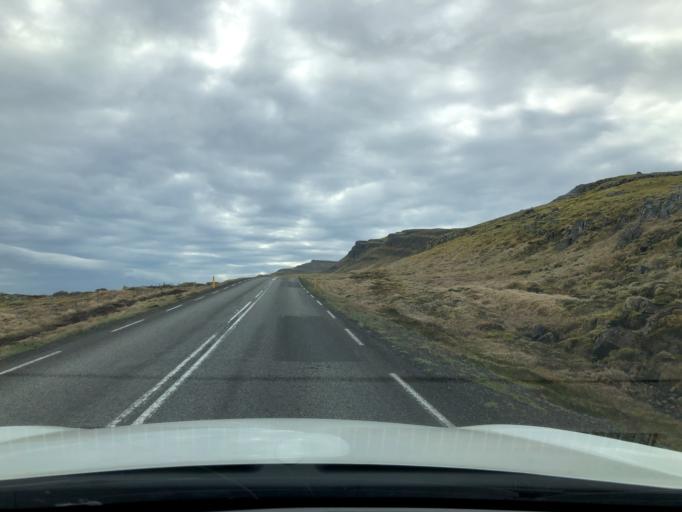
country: IS
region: East
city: Eskifjoerdur
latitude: 64.8915
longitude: -13.8432
